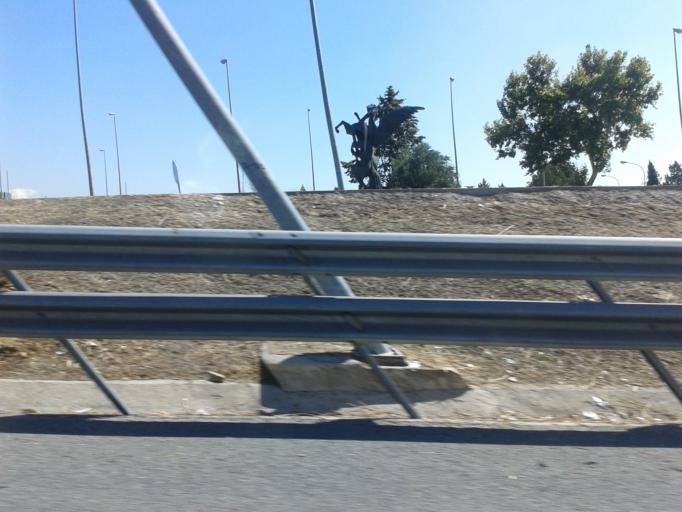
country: ES
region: Madrid
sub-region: Provincia de Madrid
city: Barajas de Madrid
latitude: 40.4703
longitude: -3.5748
